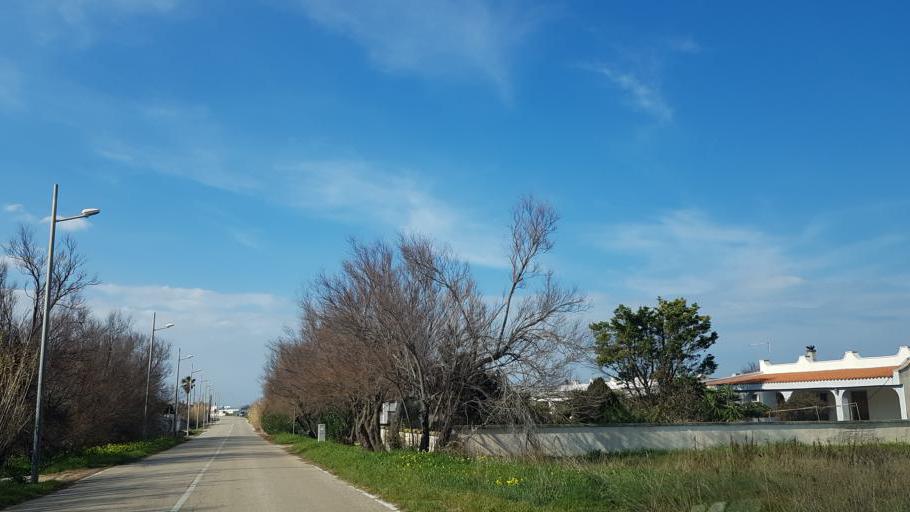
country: IT
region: Apulia
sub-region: Provincia di Brindisi
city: Brindisi
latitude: 40.6916
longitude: 17.8363
